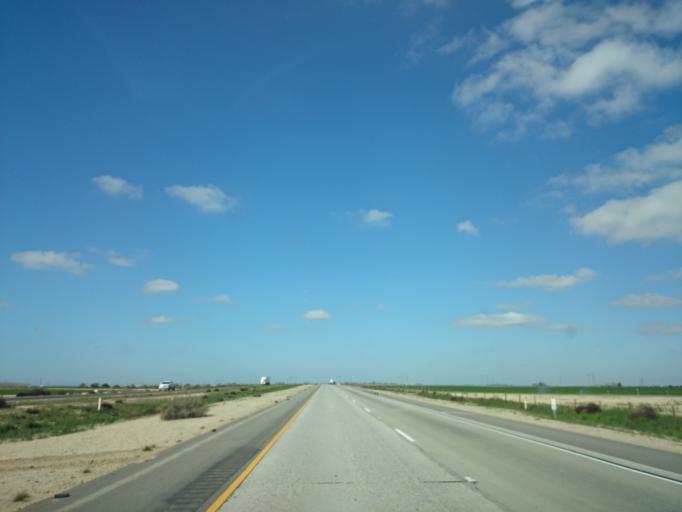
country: US
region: California
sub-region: Kern County
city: Buttonwillow
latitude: 35.3685
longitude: -119.3549
